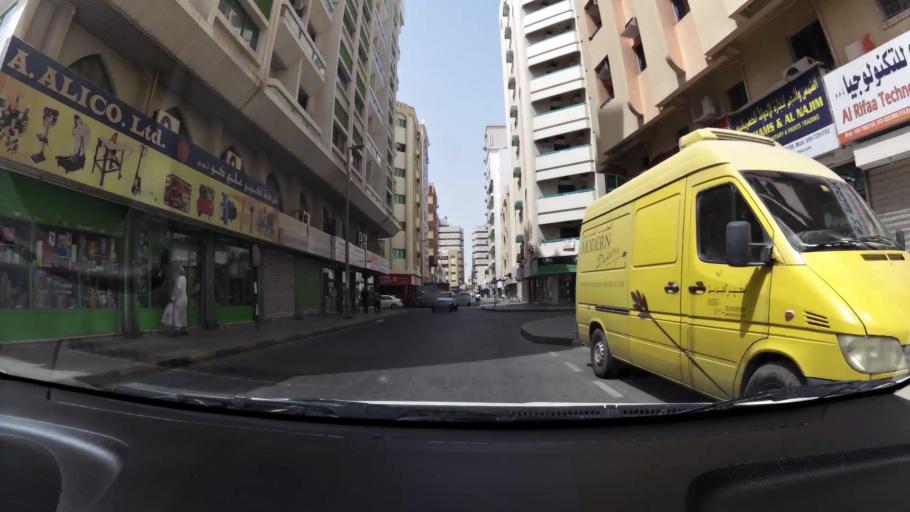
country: AE
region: Ash Shariqah
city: Sharjah
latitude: 25.3602
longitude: 55.3887
